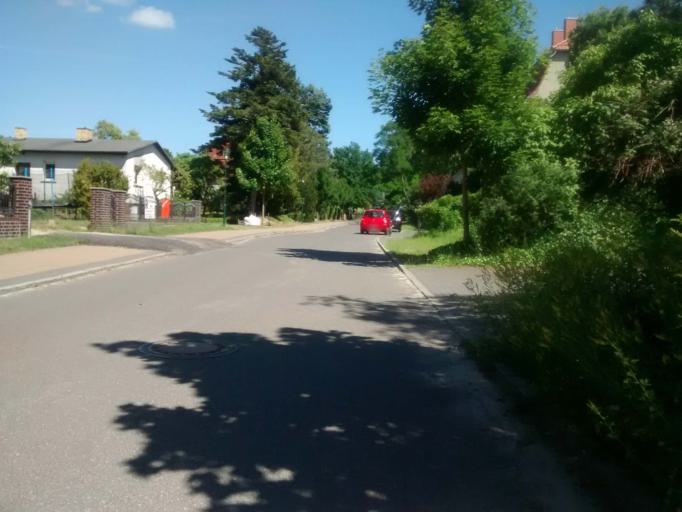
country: DE
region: Brandenburg
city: Hohen Neuendorf
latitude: 52.6786
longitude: 13.2717
